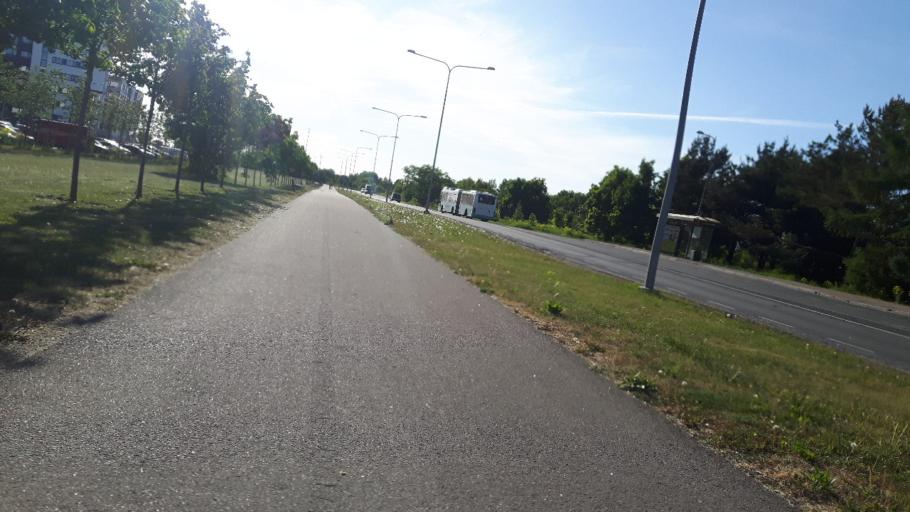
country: EE
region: Harju
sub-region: Tallinna linn
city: Kose
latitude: 59.4518
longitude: 24.8389
